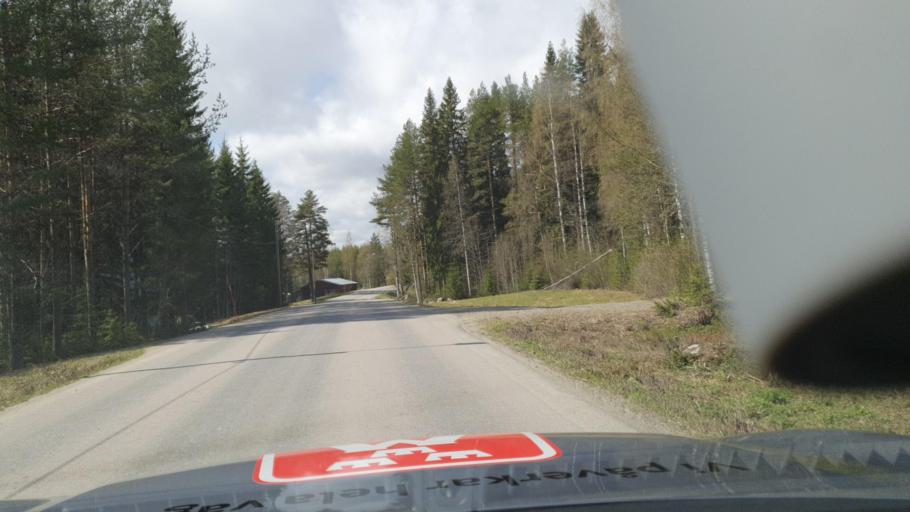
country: SE
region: Vaesternorrland
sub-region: OErnskoeldsviks Kommun
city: Ornskoldsvik
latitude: 63.6926
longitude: 18.8511
